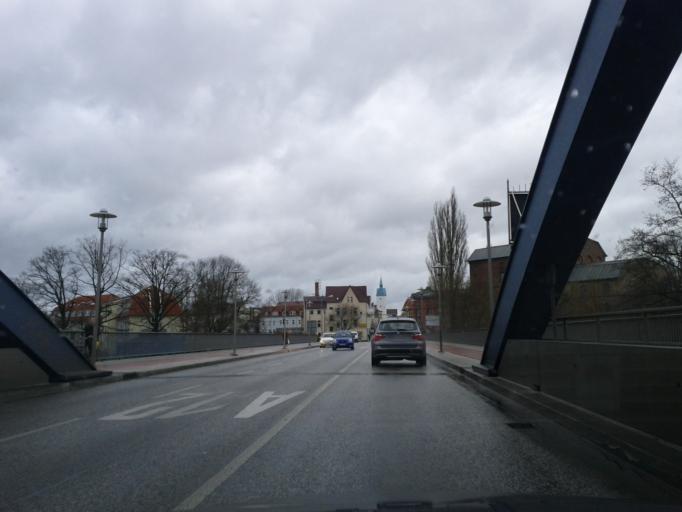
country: DE
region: Brandenburg
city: Furstenwalde
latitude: 52.3547
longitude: 14.0625
